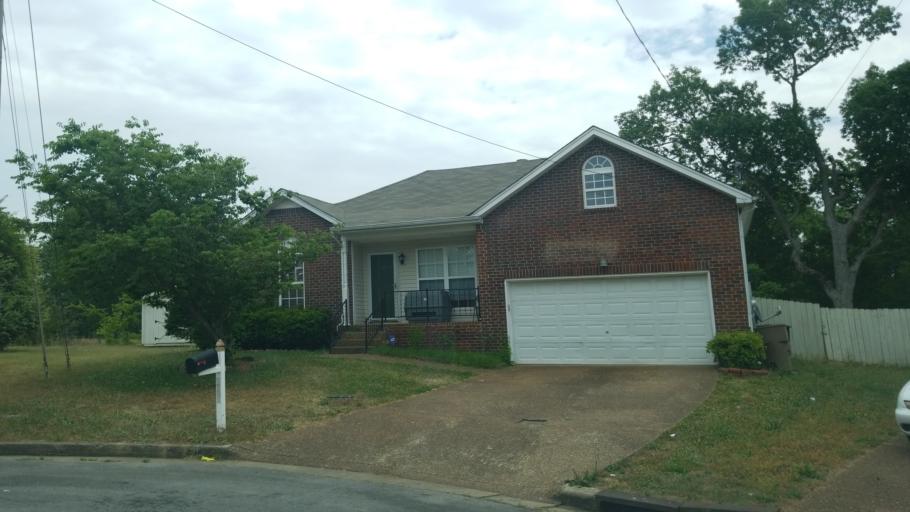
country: US
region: Tennessee
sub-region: Rutherford County
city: La Vergne
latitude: 36.0471
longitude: -86.5852
